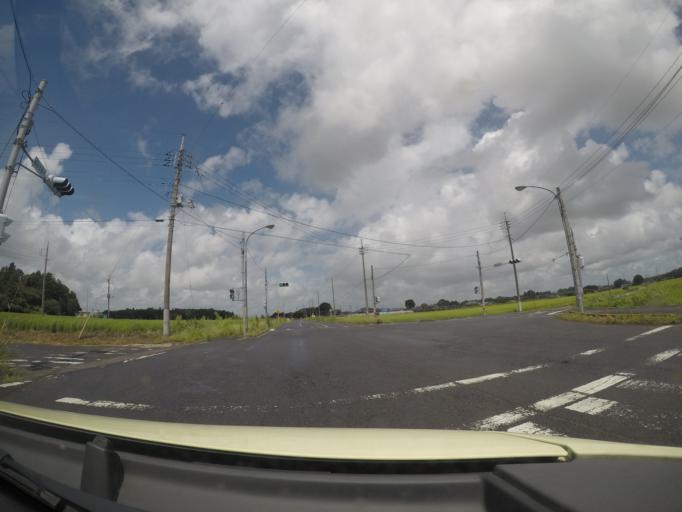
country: JP
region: Ibaraki
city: Ishige
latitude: 36.0788
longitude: 140.0212
